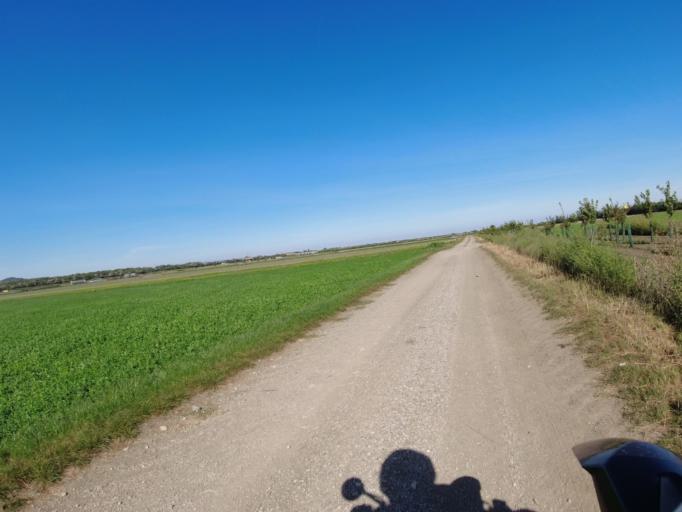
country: AT
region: Lower Austria
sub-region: Politischer Bezirk Baden
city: Trumau
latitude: 48.0190
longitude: 16.3342
